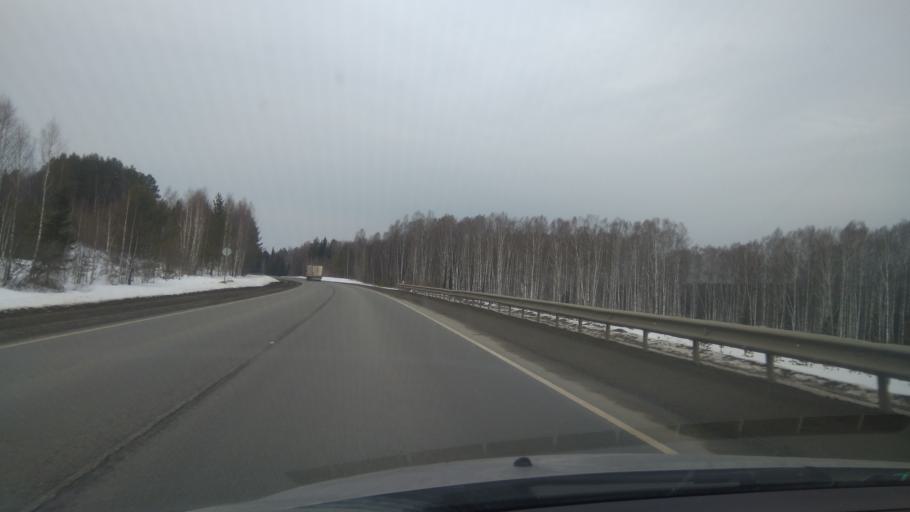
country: RU
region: Sverdlovsk
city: Ufimskiy
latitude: 56.7852
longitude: 58.3919
